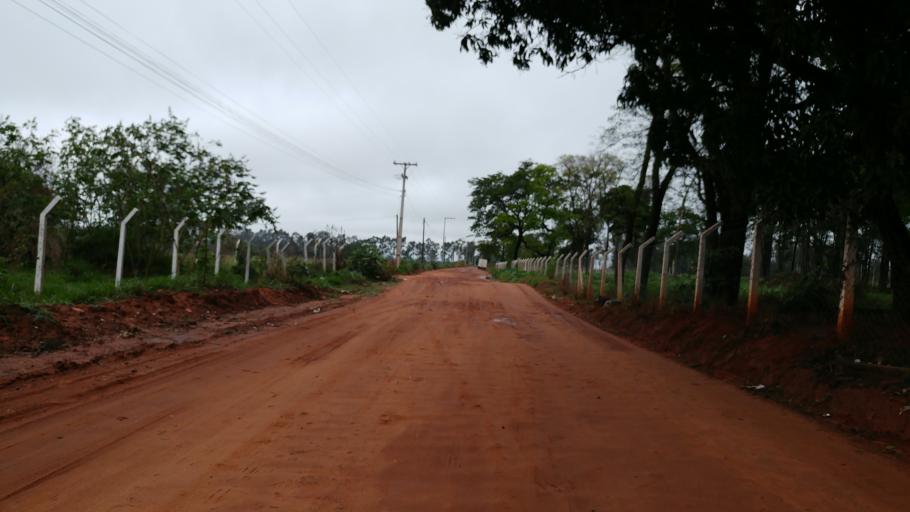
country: BR
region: Sao Paulo
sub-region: Paraguacu Paulista
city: Paraguacu Paulista
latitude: -22.4221
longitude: -50.5678
